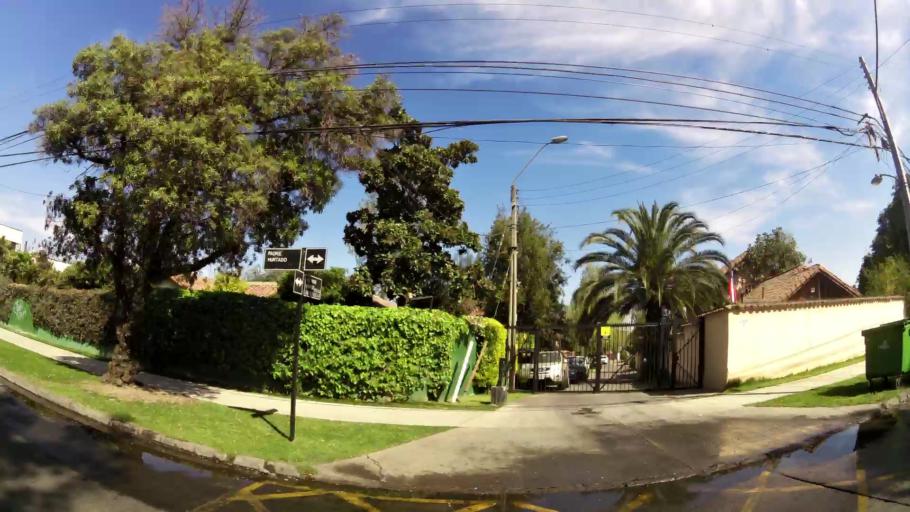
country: CL
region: Santiago Metropolitan
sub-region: Provincia de Santiago
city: Villa Presidente Frei, Nunoa, Santiago, Chile
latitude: -33.4345
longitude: -70.5373
